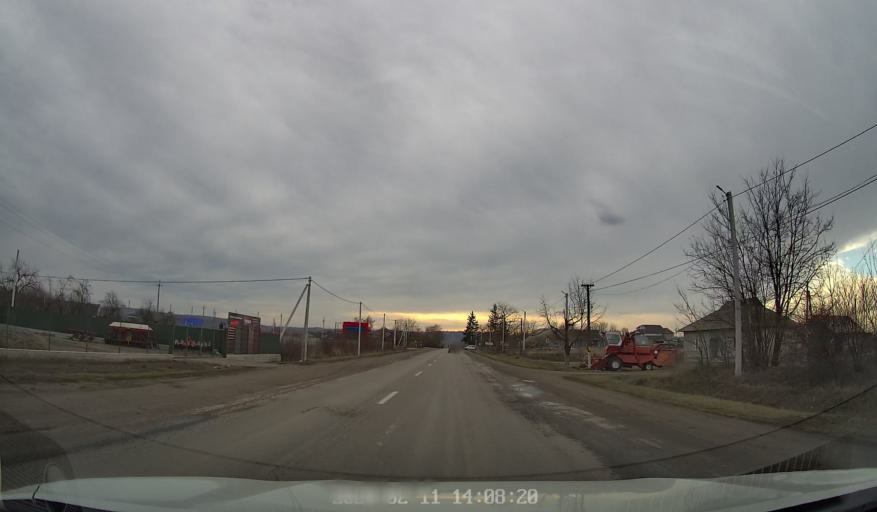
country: RO
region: Botosani
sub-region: Comuna Darabani
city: Bajura
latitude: 48.2382
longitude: 26.5471
